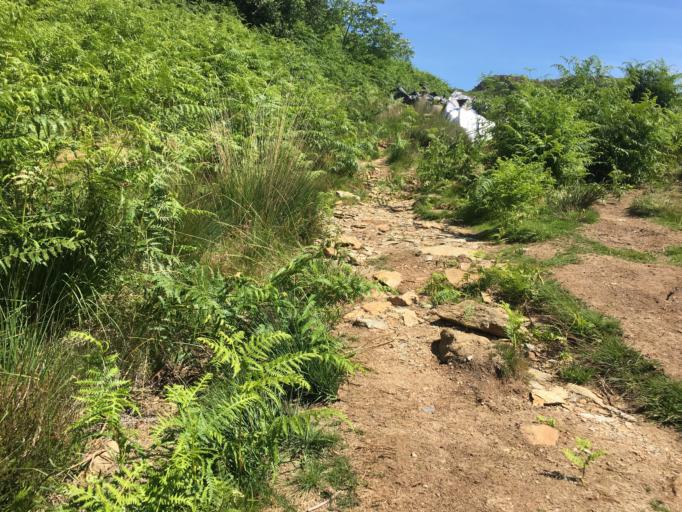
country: GB
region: Wales
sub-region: Gwynedd
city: Penrhyndeudraeth
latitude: 52.9999
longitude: -4.0883
